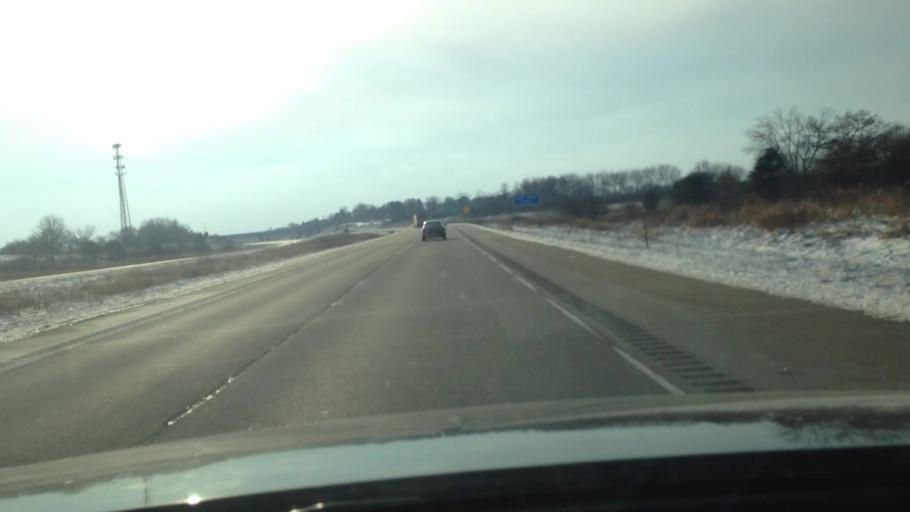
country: US
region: Wisconsin
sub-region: Walworth County
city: East Troy
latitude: 42.7479
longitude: -88.4456
